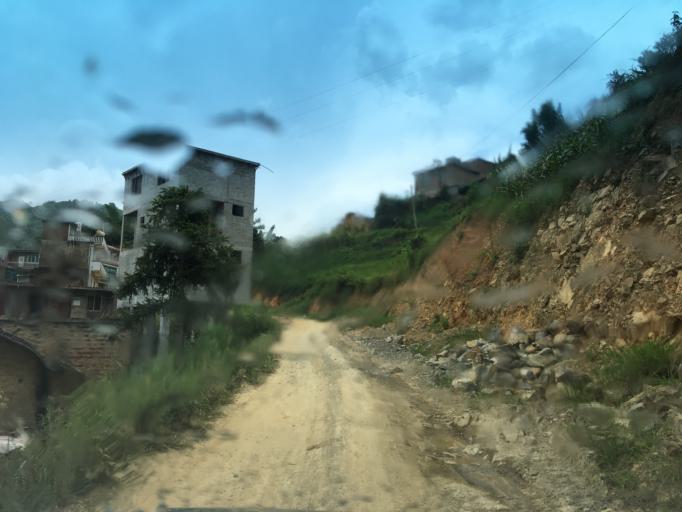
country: CN
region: Guangxi Zhuangzu Zizhiqu
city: Leli
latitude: 24.8017
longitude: 105.9767
